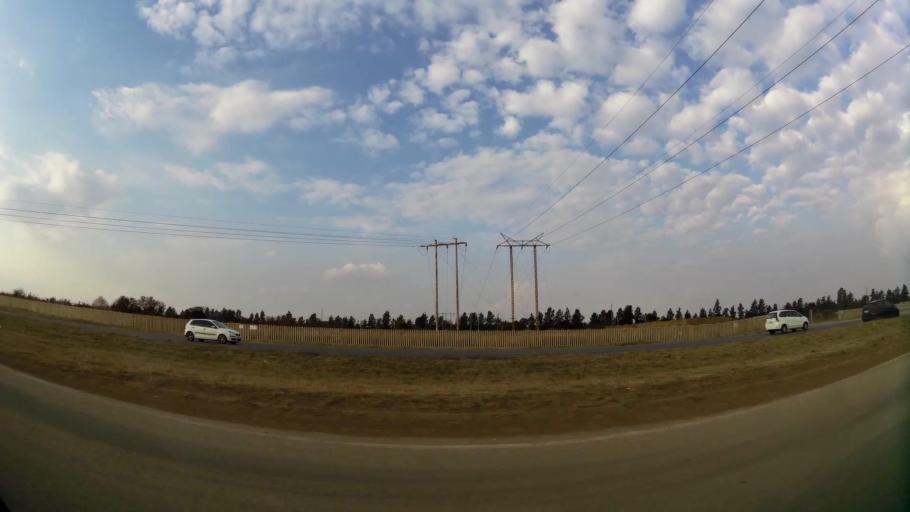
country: ZA
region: Gauteng
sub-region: Sedibeng District Municipality
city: Vereeniging
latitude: -26.6454
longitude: 27.8751
